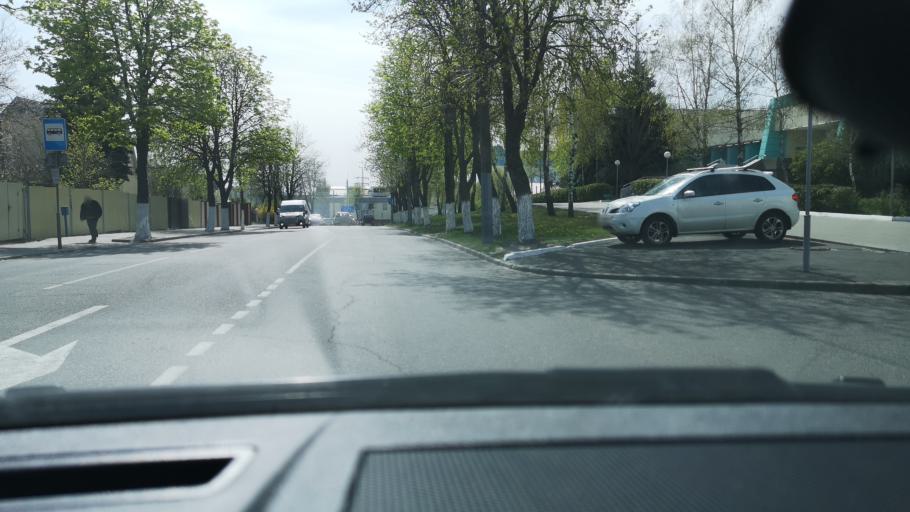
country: BY
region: Gomel
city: Gomel
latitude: 52.4158
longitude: 31.0063
